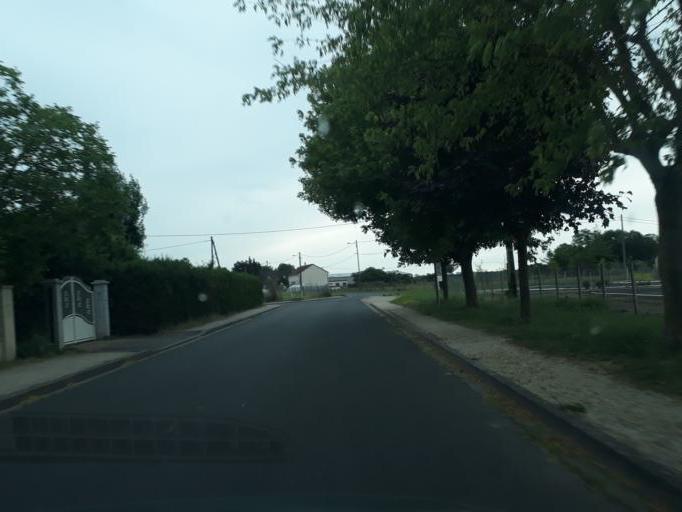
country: FR
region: Centre
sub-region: Departement du Loiret
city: Saint-Denis-en-Val
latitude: 47.8747
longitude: 1.9548
